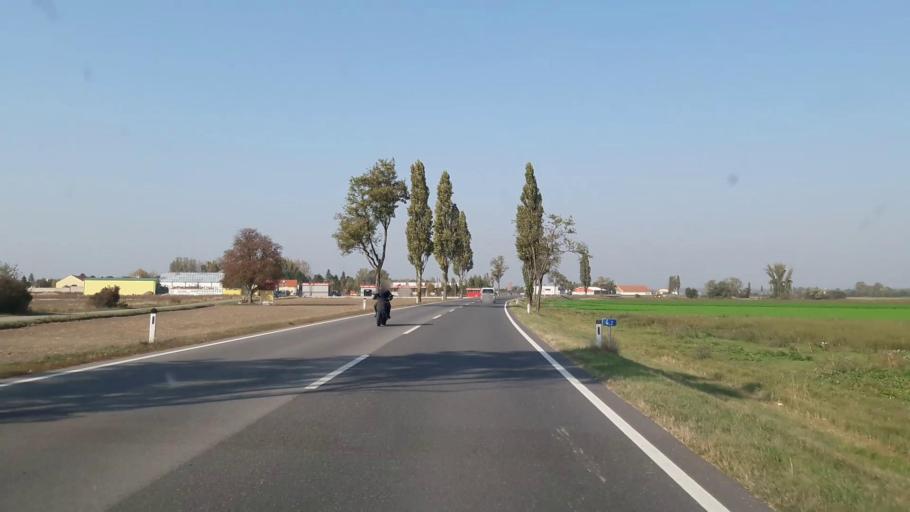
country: AT
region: Lower Austria
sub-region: Politischer Bezirk Ganserndorf
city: Engelhartstetten
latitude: 48.1740
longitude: 16.8914
